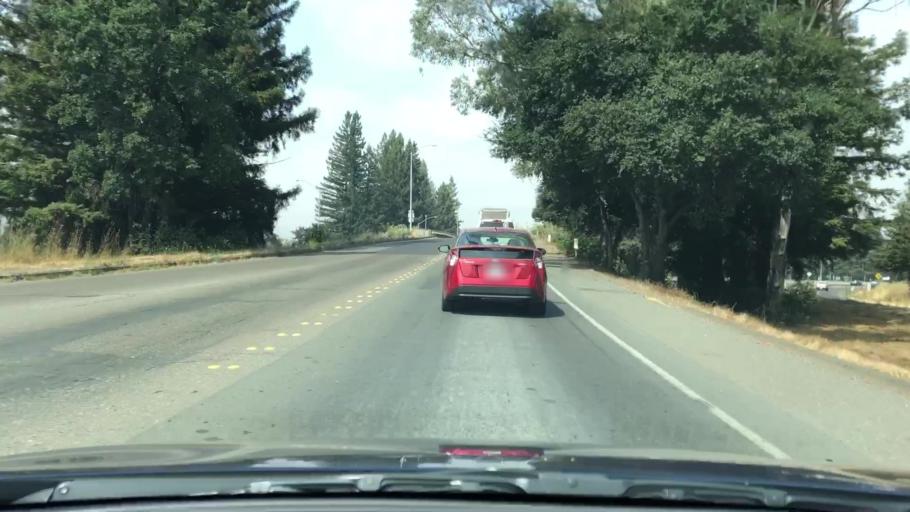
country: US
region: California
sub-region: Sonoma County
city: Larkfield-Wikiup
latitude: 38.4962
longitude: -122.7546
